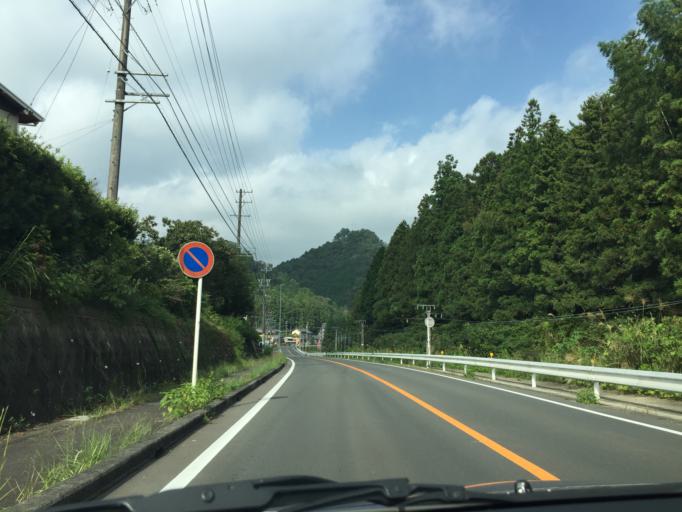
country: JP
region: Aichi
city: Shinshiro
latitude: 34.9363
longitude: 137.5877
